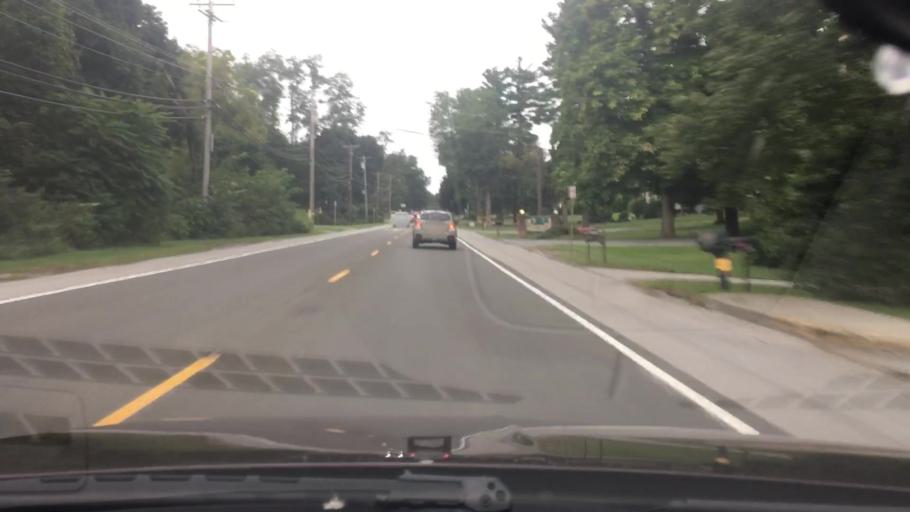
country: US
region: New York
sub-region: Dutchess County
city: Pleasant Valley
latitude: 41.7333
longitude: -73.8369
